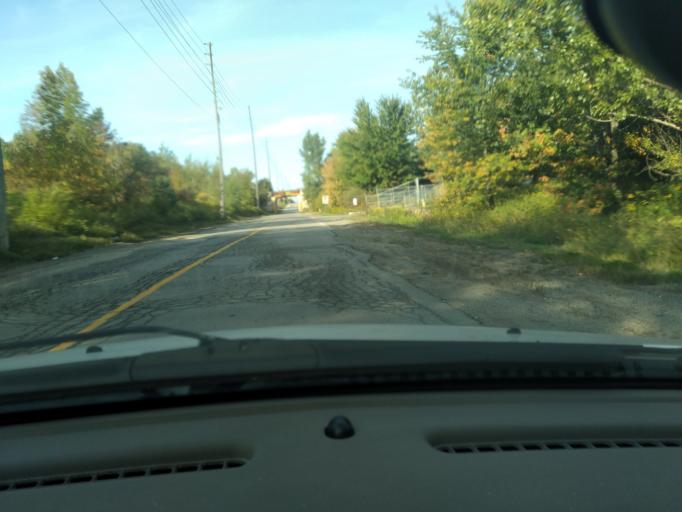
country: CA
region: Ontario
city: Innisfil
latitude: 44.3268
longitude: -79.6672
